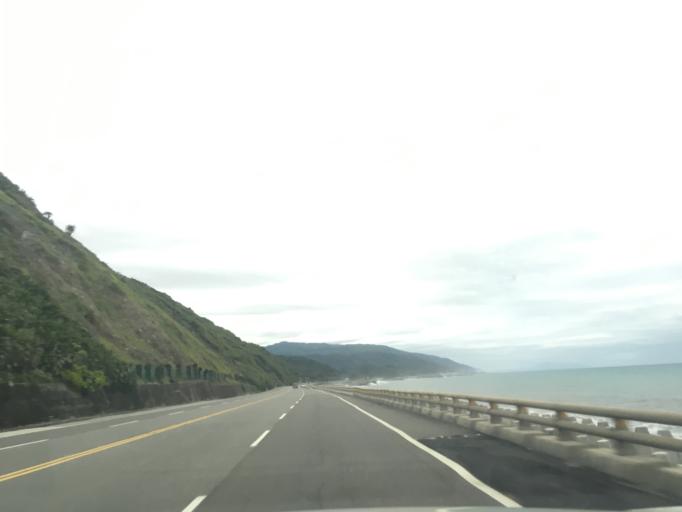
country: TW
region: Taiwan
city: Hengchun
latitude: 22.3151
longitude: 120.8914
